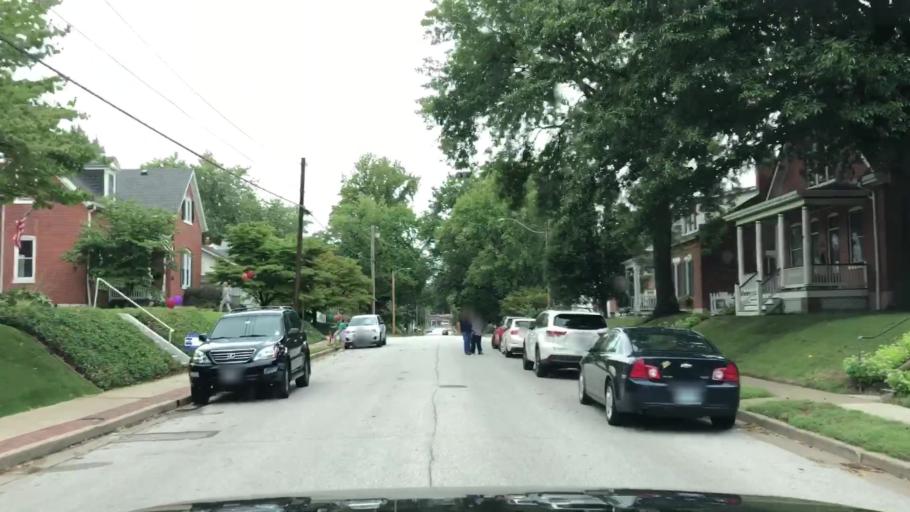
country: US
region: Missouri
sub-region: Saint Charles County
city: Saint Charles
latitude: 38.7854
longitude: -90.4882
